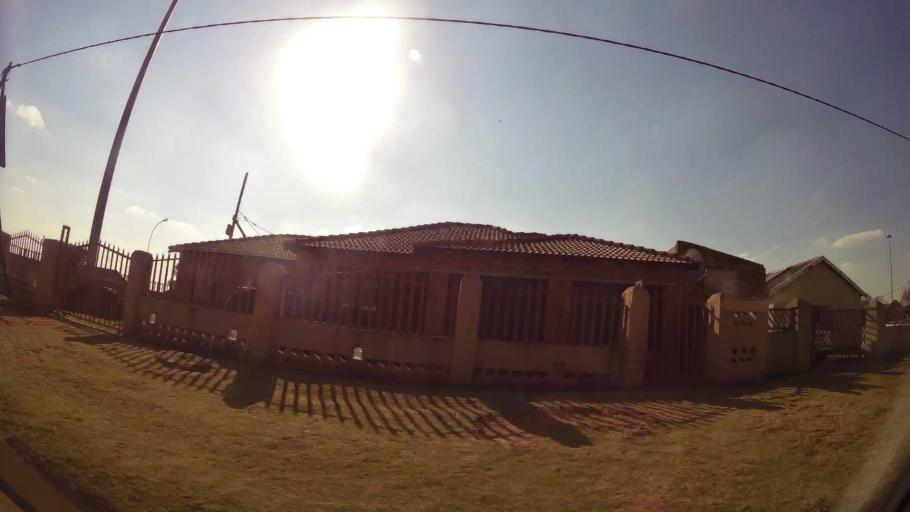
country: ZA
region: Gauteng
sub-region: Ekurhuleni Metropolitan Municipality
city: Benoni
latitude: -26.2318
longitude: 28.3238
